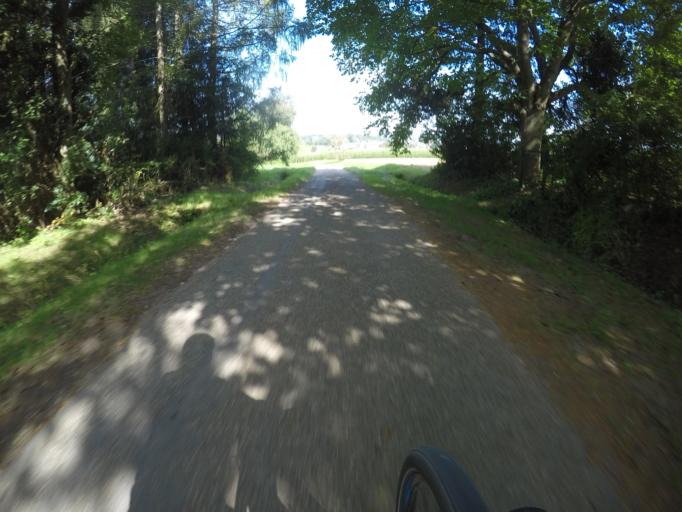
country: DE
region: Baden-Wuerttemberg
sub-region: Karlsruhe Region
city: Muhlacker
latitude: 48.9282
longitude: 8.8416
